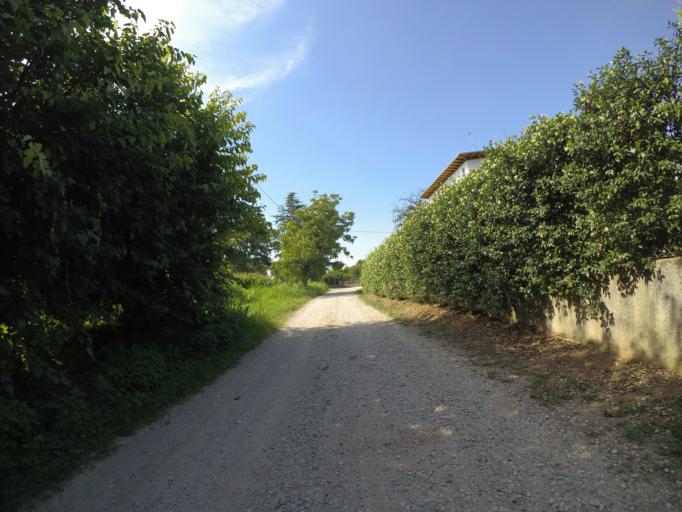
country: IT
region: Friuli Venezia Giulia
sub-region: Provincia di Udine
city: Mortegliano
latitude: 45.9499
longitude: 13.1640
